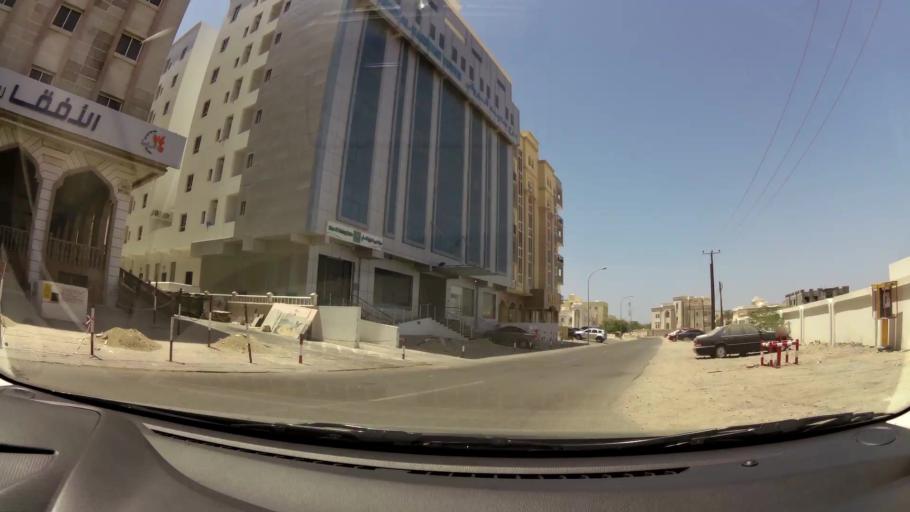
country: OM
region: Muhafazat Masqat
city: Bawshar
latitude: 23.5901
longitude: 58.3850
